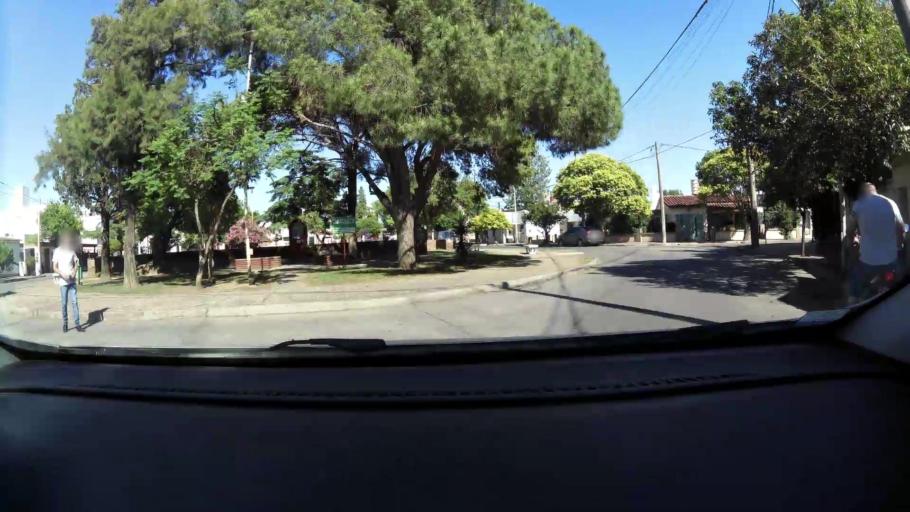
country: AR
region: Cordoba
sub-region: Departamento de Capital
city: Cordoba
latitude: -31.4394
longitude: -64.1635
